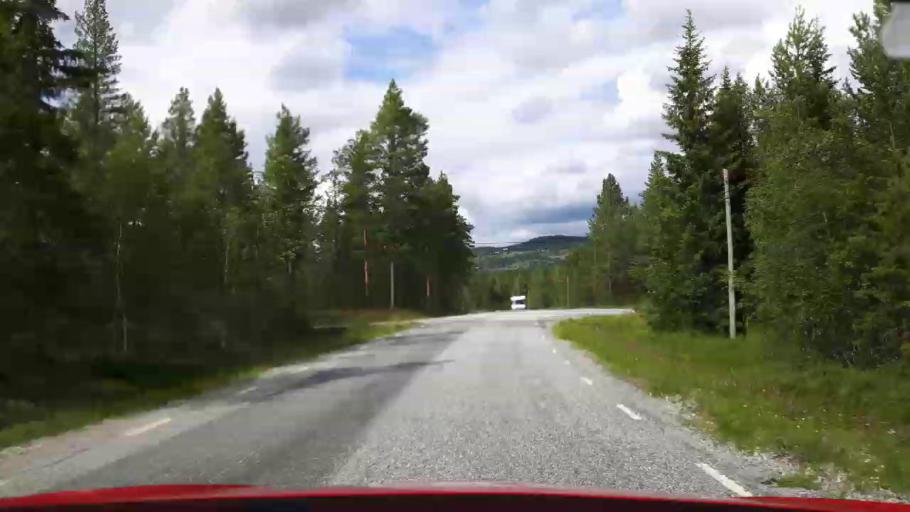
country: NO
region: Hedmark
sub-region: Engerdal
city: Engerdal
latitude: 62.4241
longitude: 12.6883
